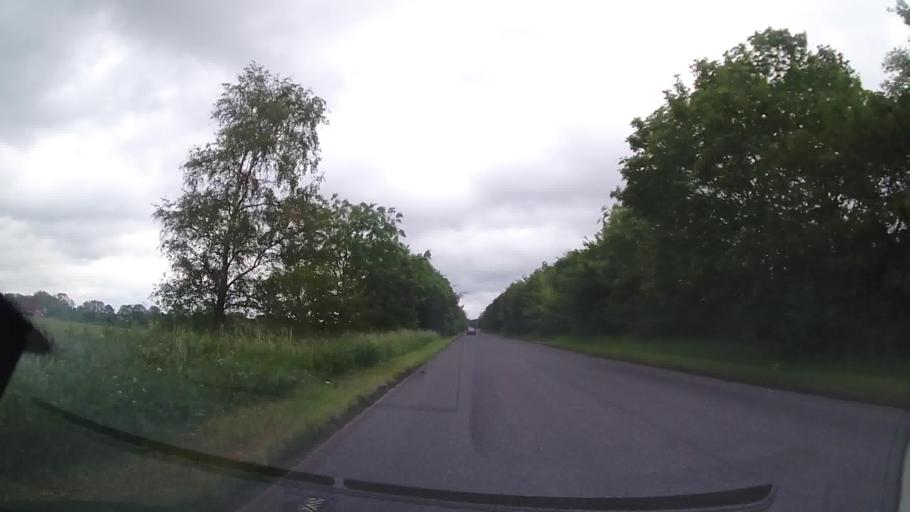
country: GB
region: England
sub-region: Shropshire
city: Market Drayton
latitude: 52.8989
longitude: -2.5173
